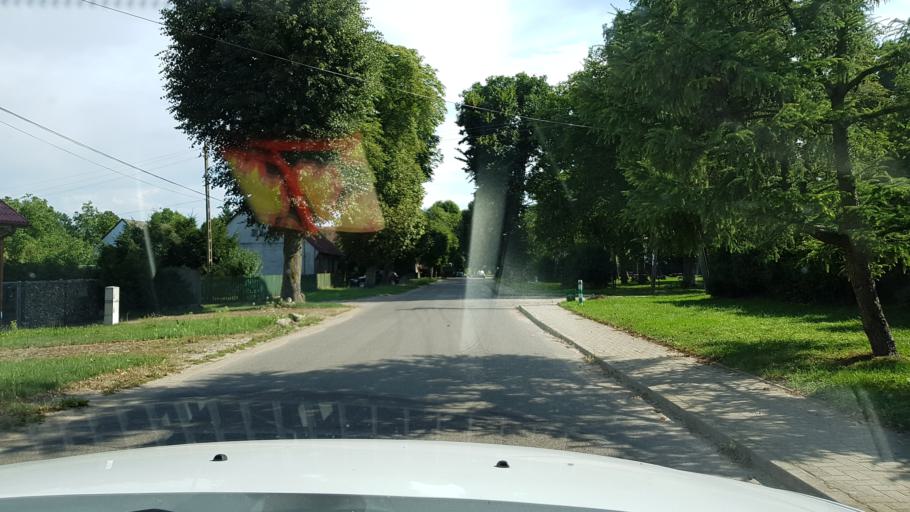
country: PL
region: West Pomeranian Voivodeship
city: Trzcinsko Zdroj
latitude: 52.9550
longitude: 14.5490
